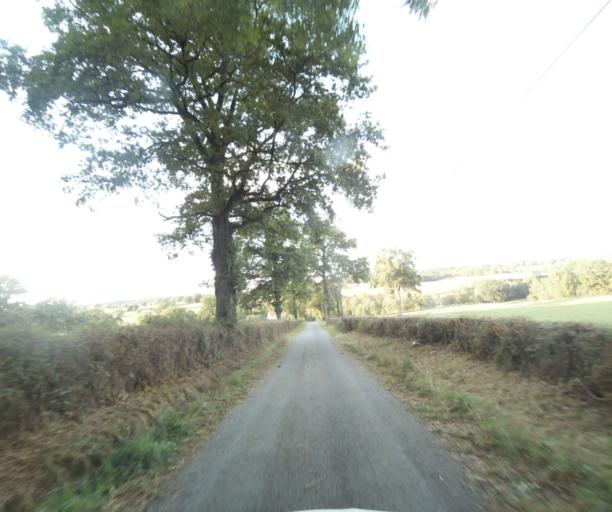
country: FR
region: Bourgogne
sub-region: Departement de Saone-et-Loire
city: Charolles
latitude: 46.4443
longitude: 4.3608
